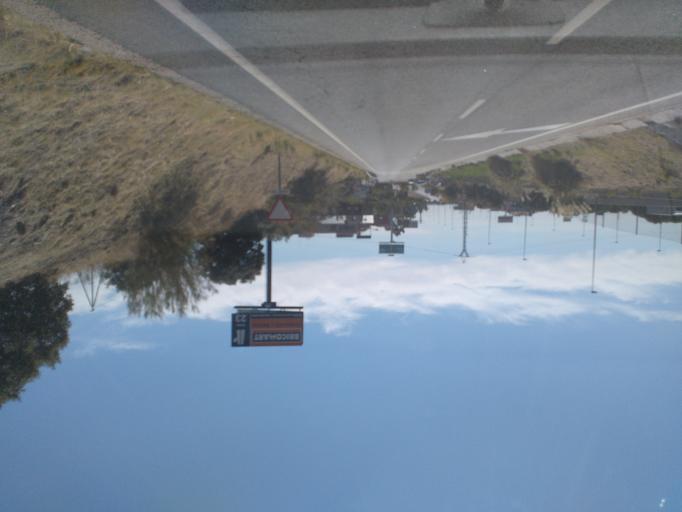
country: ES
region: Madrid
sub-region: Provincia de Madrid
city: Las Matas
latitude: 40.5589
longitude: -3.9018
